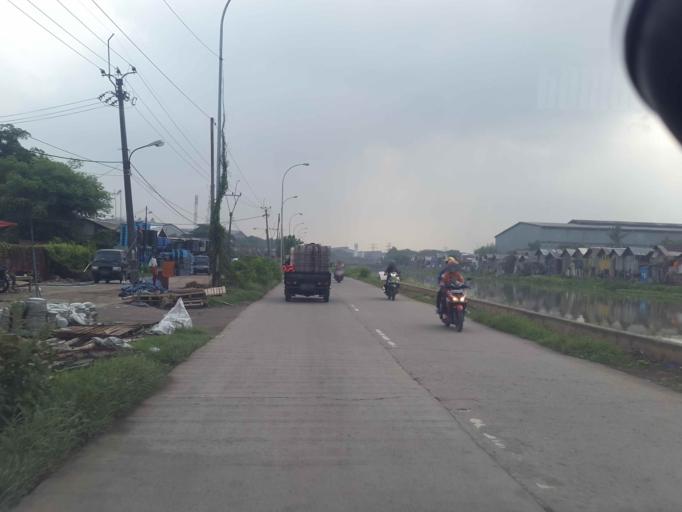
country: ID
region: West Java
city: Cikarang
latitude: -6.2840
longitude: 107.1085
